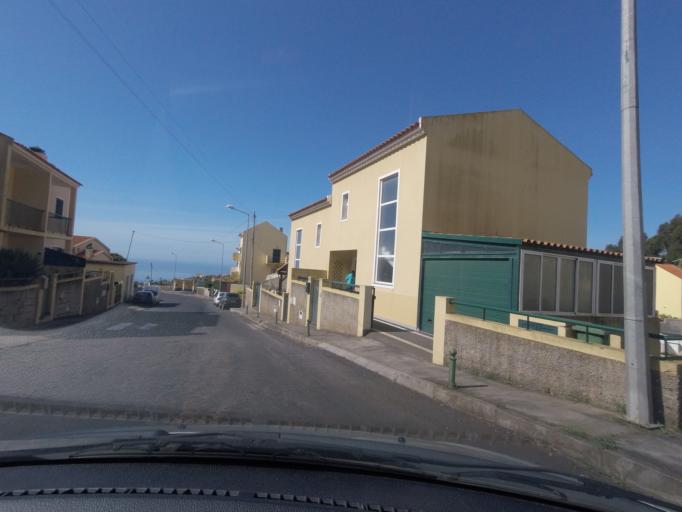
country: PT
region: Madeira
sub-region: Santa Cruz
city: Camacha
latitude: 32.6584
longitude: -16.8556
